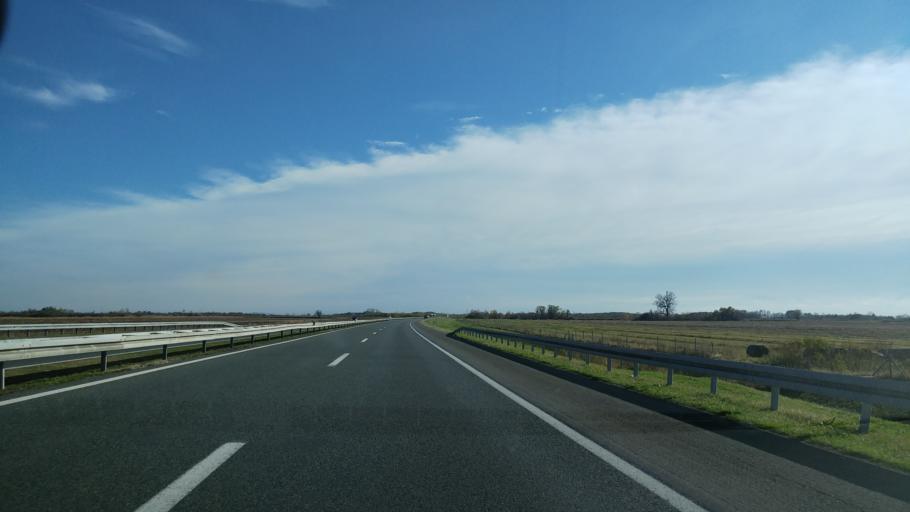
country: HR
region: Brodsko-Posavska
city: Okucani
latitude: 45.2602
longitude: 17.1645
